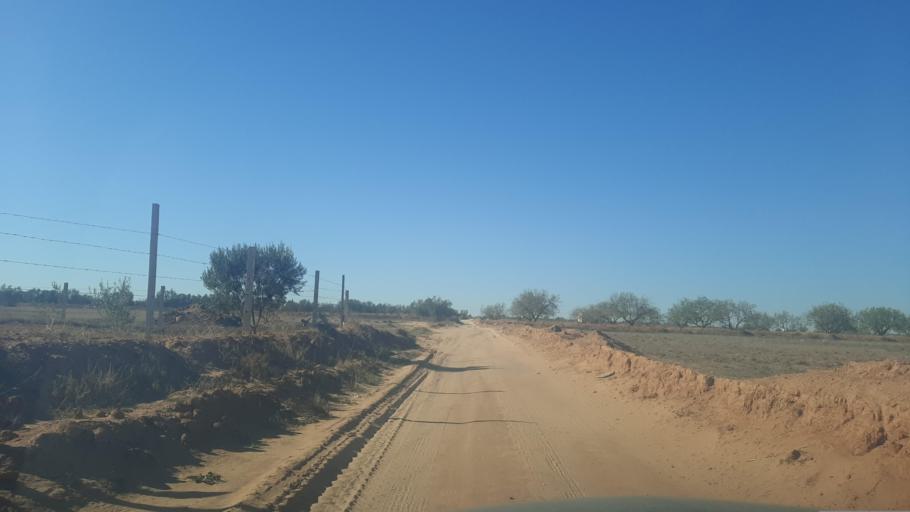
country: TN
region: Safaqis
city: Sfax
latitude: 34.8952
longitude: 10.5969
